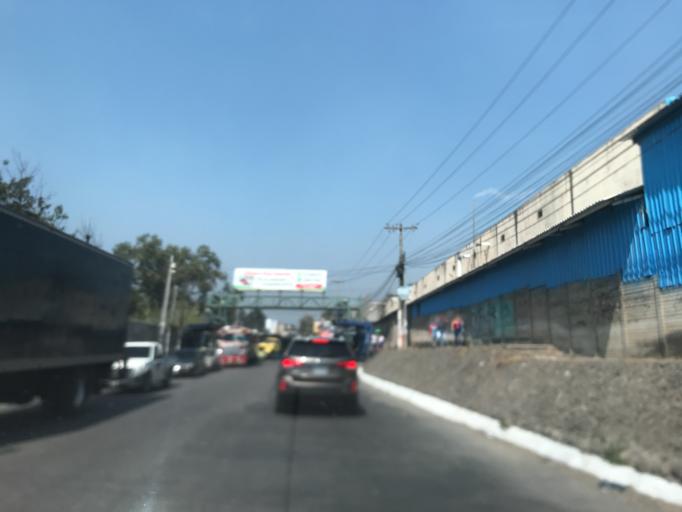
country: GT
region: Guatemala
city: Villa Nueva
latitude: 14.5389
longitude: -90.5564
